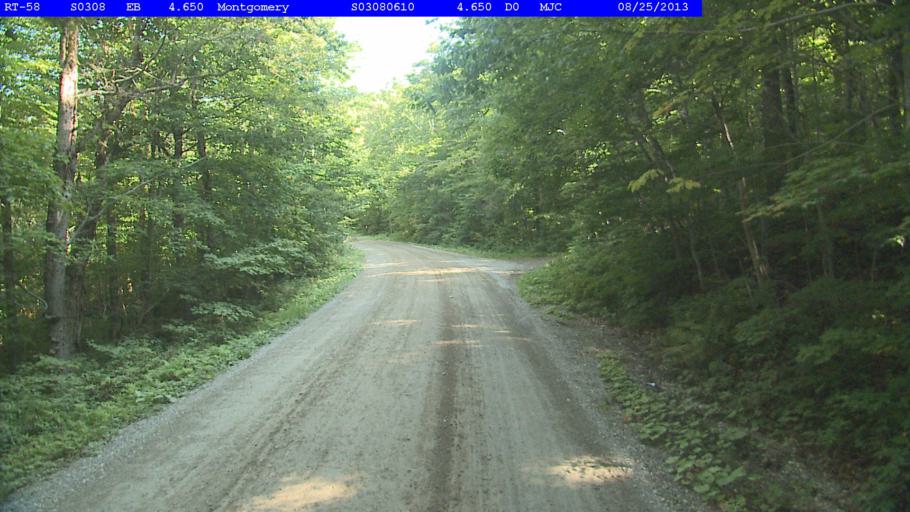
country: US
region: Vermont
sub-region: Franklin County
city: Richford
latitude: 44.8428
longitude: -72.5353
